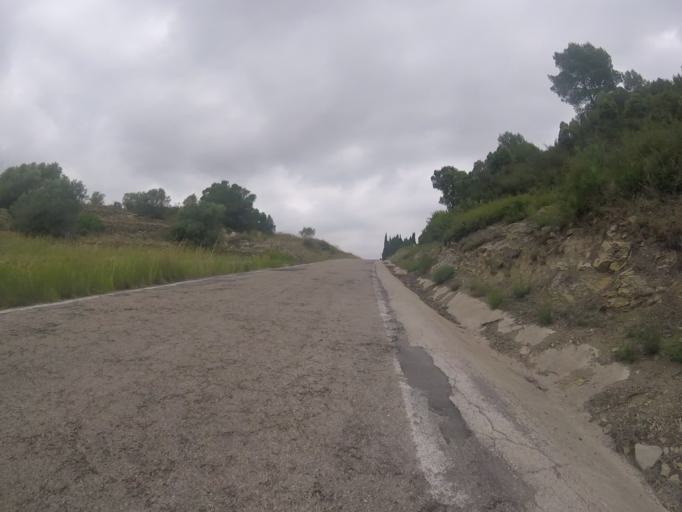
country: ES
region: Valencia
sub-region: Provincia de Castello
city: Cabanes
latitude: 40.1219
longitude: 0.0453
